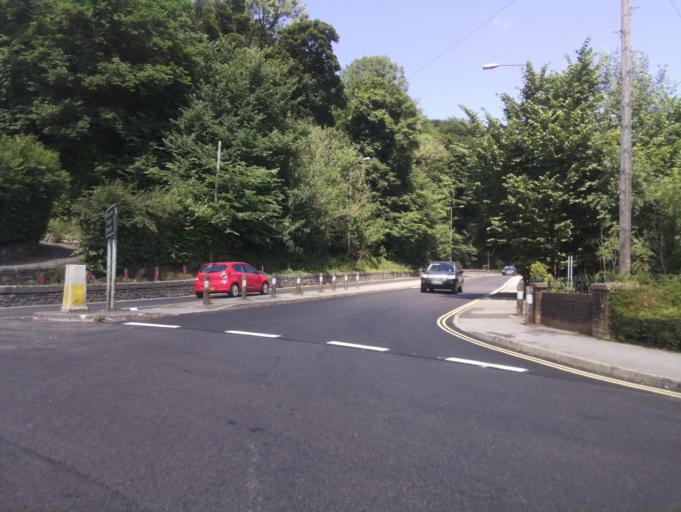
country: GB
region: England
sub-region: Derbyshire
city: Buxton
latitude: 53.2540
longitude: -1.9043
